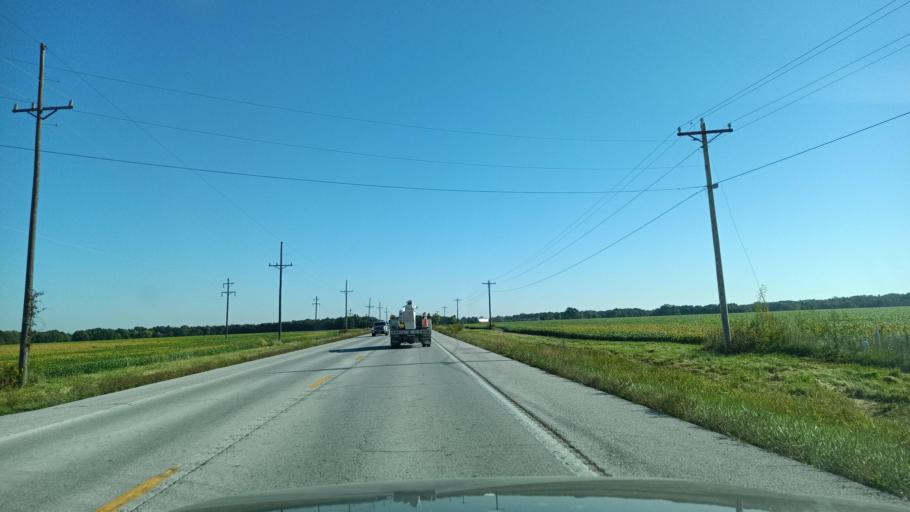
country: US
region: Missouri
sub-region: Audrain County
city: Vandalia
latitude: 39.4548
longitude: -91.6201
